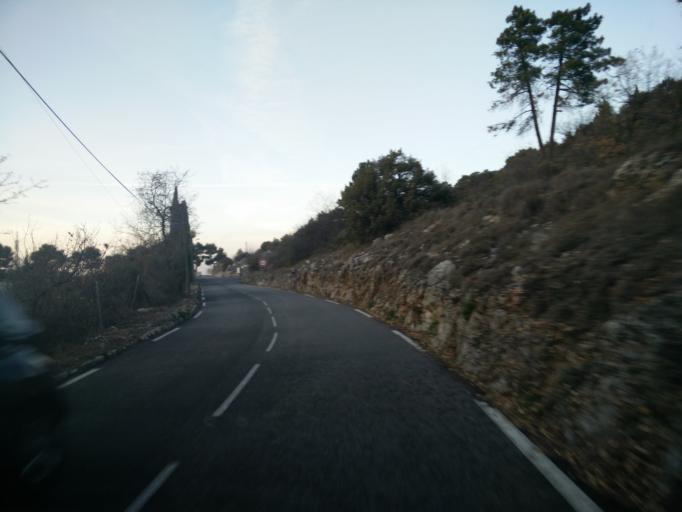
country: FR
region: Provence-Alpes-Cote d'Azur
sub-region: Departement des Alpes-Maritimes
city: Peille
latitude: 43.7917
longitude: 7.4010
